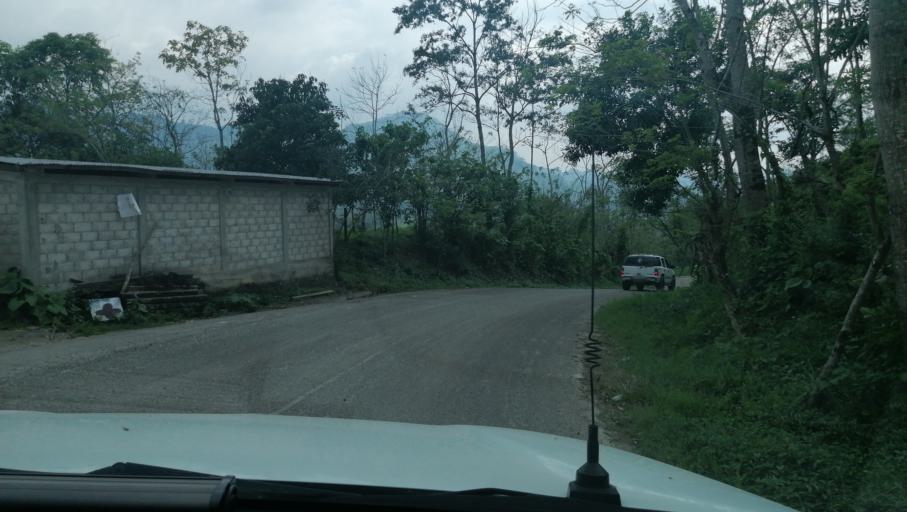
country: MX
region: Chiapas
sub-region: Francisco Leon
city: San Miguel la Sardina
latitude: 17.2255
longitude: -93.3456
